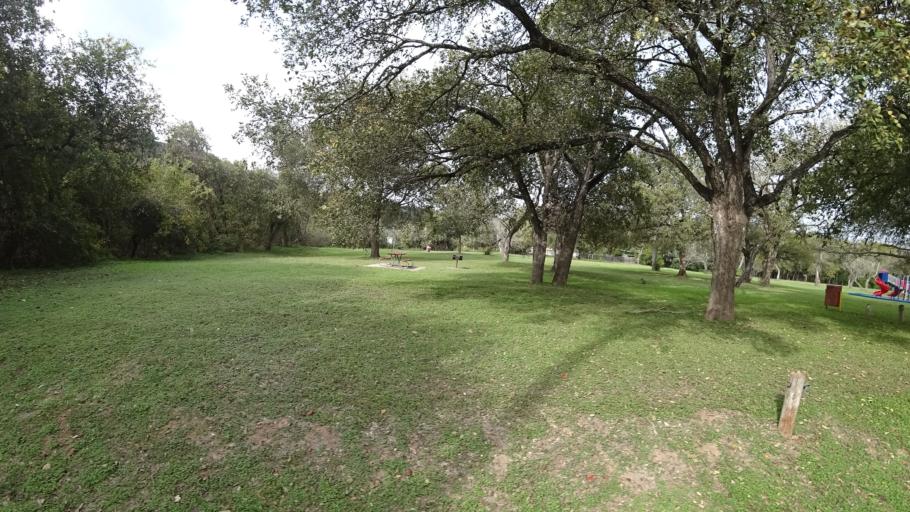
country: US
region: Texas
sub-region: Travis County
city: Hudson Bend
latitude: 30.3821
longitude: -97.9131
